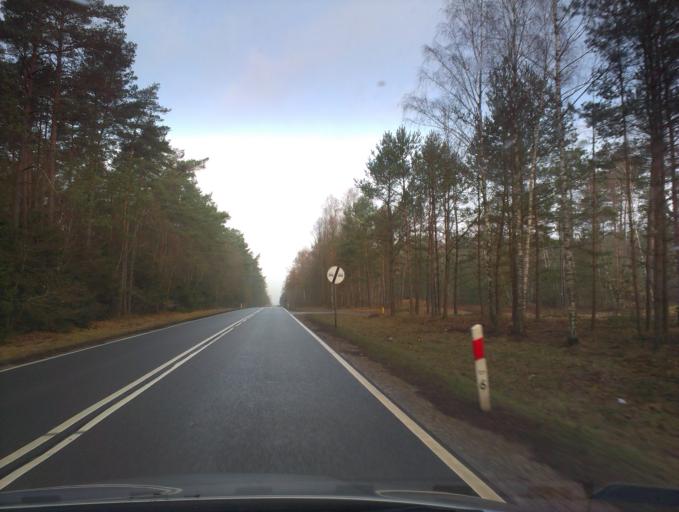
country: PL
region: West Pomeranian Voivodeship
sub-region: Powiat koszalinski
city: Sianow
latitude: 54.1112
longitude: 16.3289
